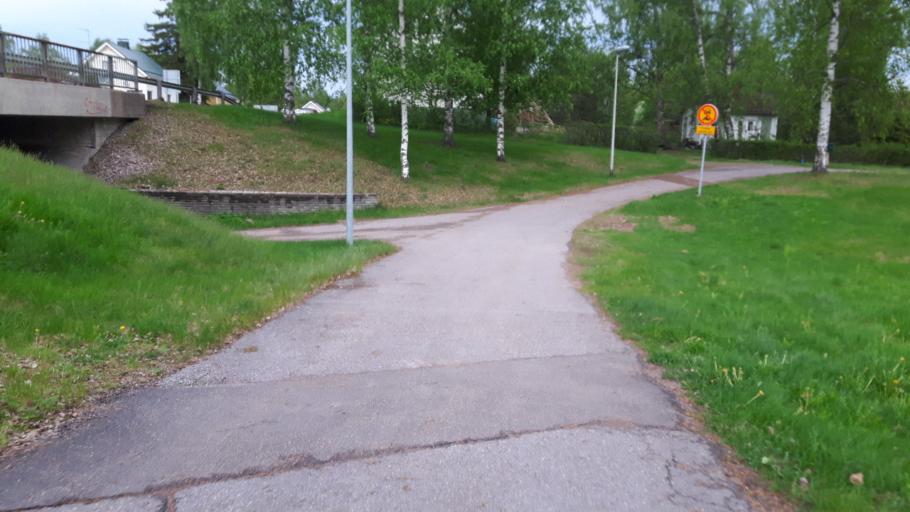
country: FI
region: Kymenlaakso
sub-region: Kotka-Hamina
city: Hamina
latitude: 60.5617
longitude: 27.2164
